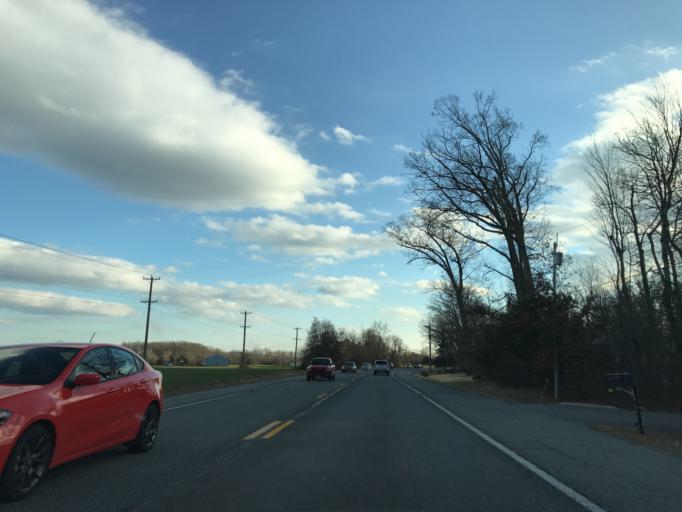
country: US
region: Maryland
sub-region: Cecil County
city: North East
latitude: 39.6564
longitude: -75.9532
